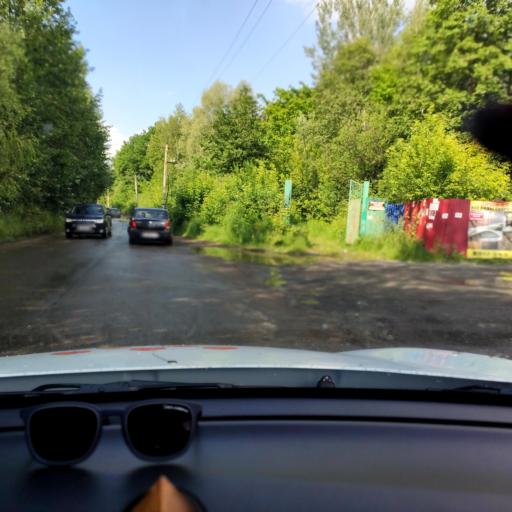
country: RU
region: Tatarstan
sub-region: Zelenodol'skiy Rayon
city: Vasil'yevo
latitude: 55.8271
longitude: 48.7687
